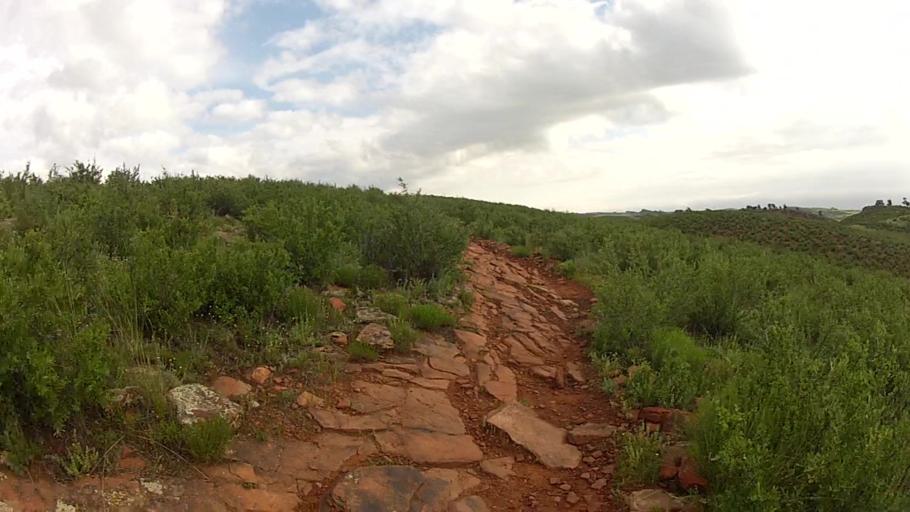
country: US
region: Colorado
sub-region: Larimer County
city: Loveland
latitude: 40.4400
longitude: -105.1562
